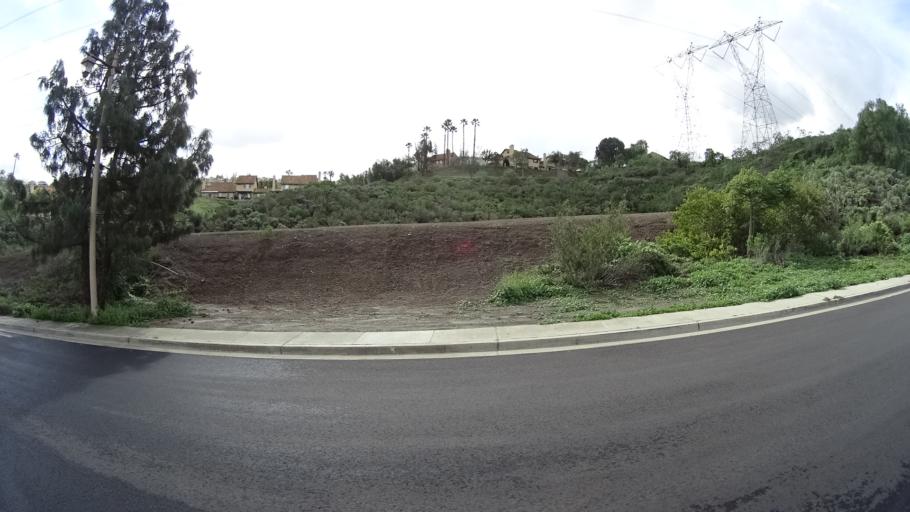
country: US
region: California
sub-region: Orange County
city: Villa Park
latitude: 33.8403
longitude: -117.7791
